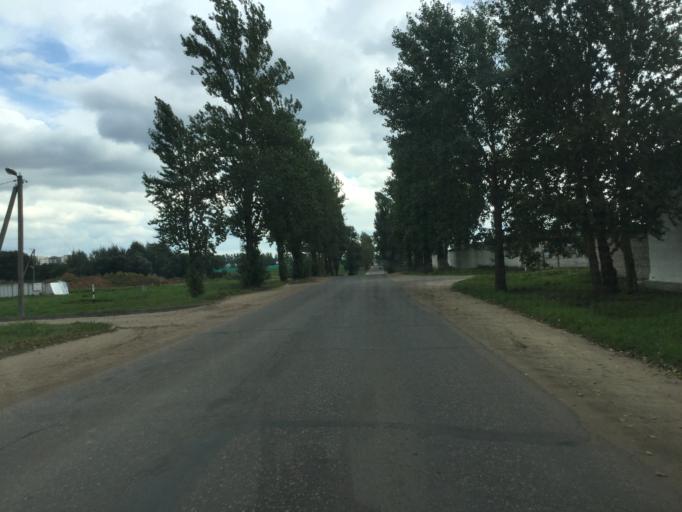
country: BY
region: Vitebsk
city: Vitebsk
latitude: 55.1649
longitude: 30.2561
